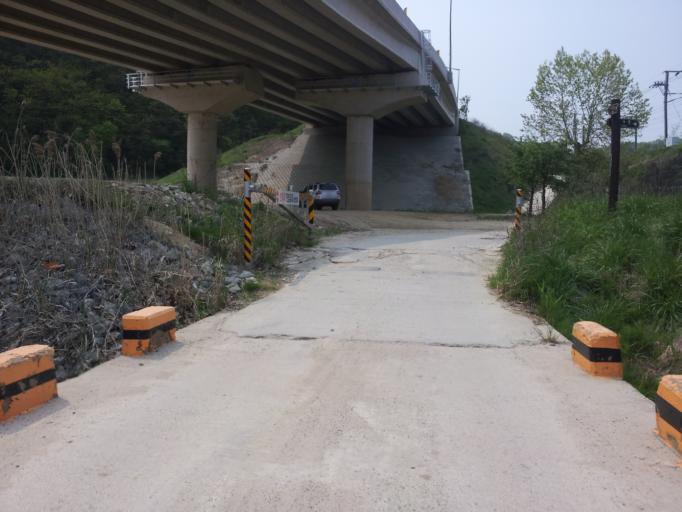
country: KR
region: Daejeon
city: Daejeon
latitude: 36.2749
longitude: 127.3459
